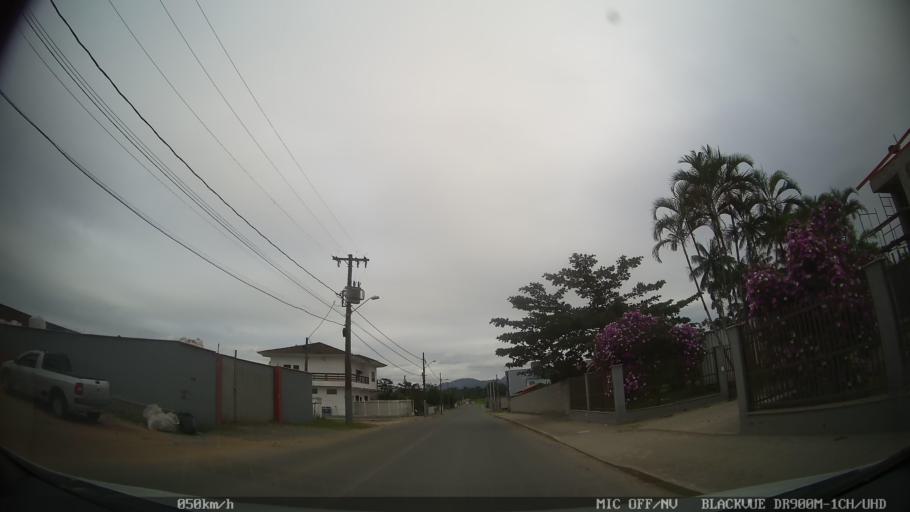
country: BR
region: Santa Catarina
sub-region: Joinville
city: Joinville
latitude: -26.3339
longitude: -48.9081
